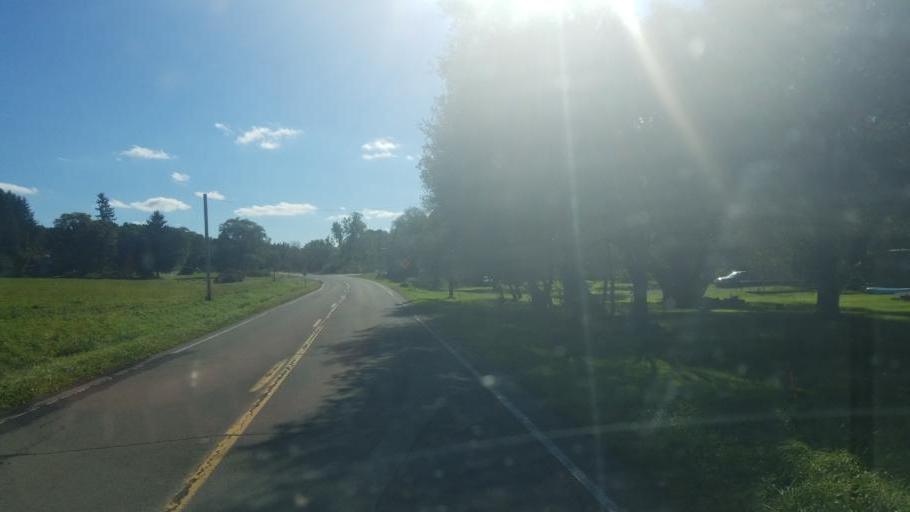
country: US
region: New York
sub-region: Allegany County
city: Friendship
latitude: 42.2799
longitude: -78.1283
